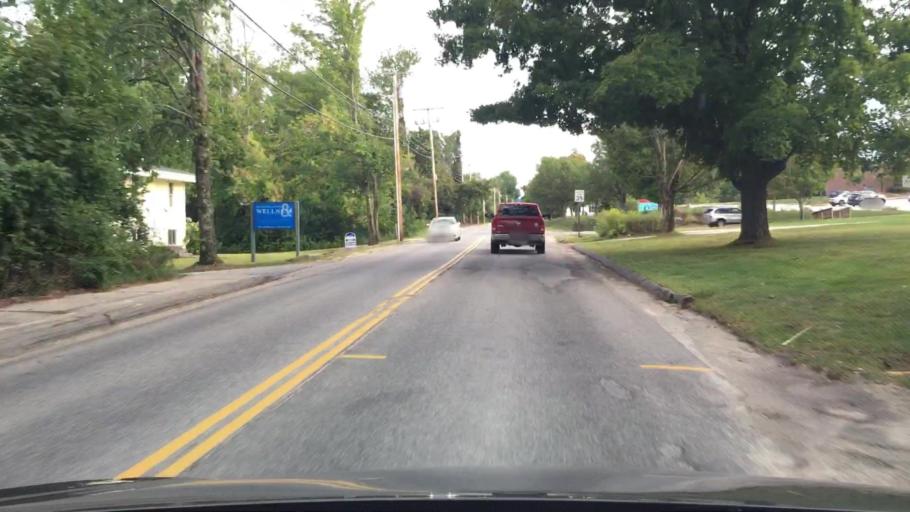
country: US
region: Maine
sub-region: Cumberland County
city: Bridgton
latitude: 44.0479
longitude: -70.7129
